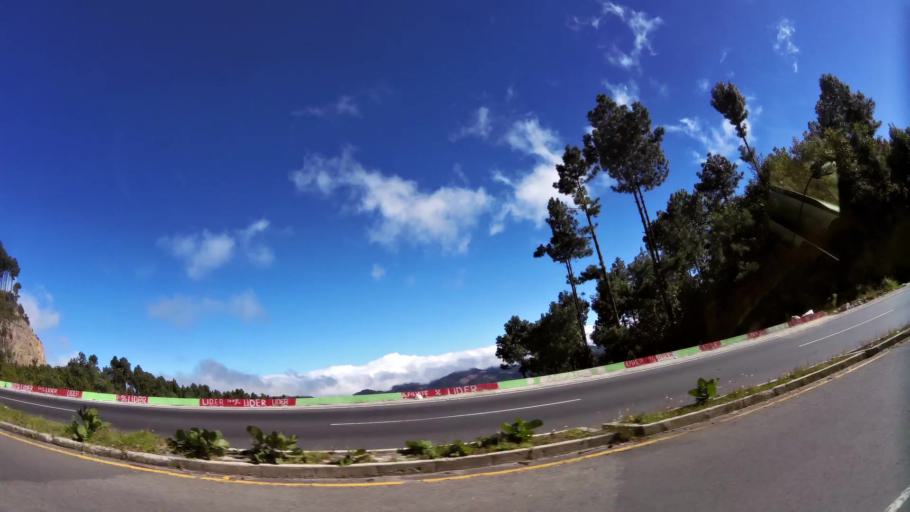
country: GT
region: Solola
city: Santa Catarina Ixtahuacan
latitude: 14.8226
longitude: -91.3510
